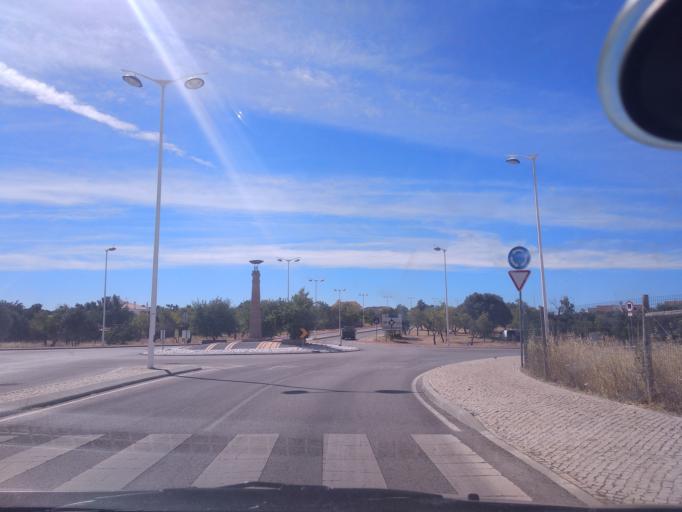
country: PT
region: Faro
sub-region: Sao Bras de Alportel
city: Sao Bras de Alportel
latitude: 37.1544
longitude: -7.8766
